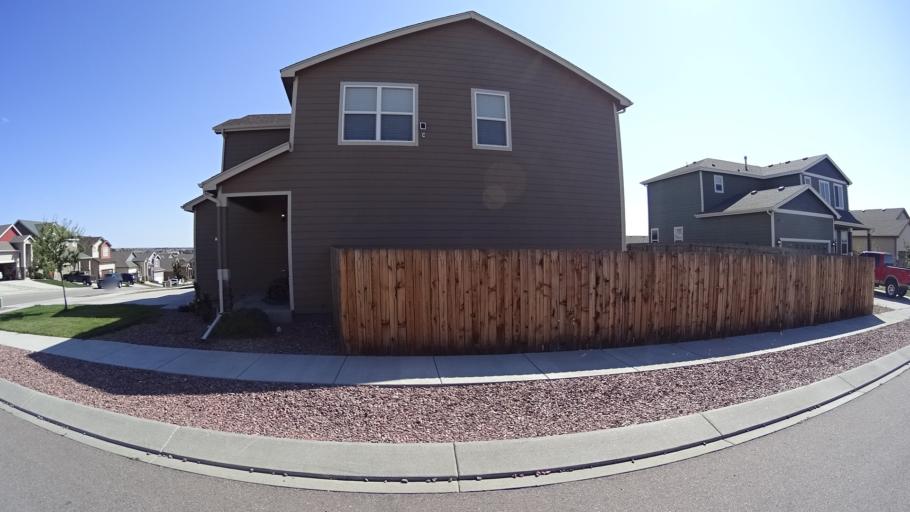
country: US
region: Colorado
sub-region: El Paso County
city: Cimarron Hills
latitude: 38.9277
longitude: -104.7089
